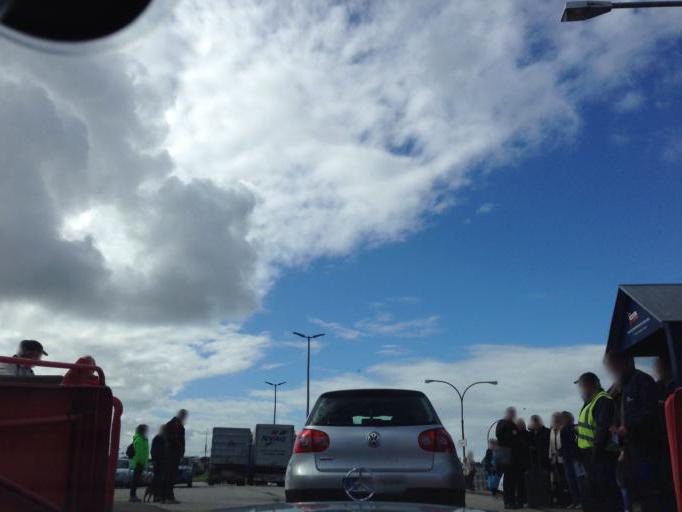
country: DE
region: Schleswig-Holstein
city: Wyk auf Fohr
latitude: 54.6931
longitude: 8.5756
